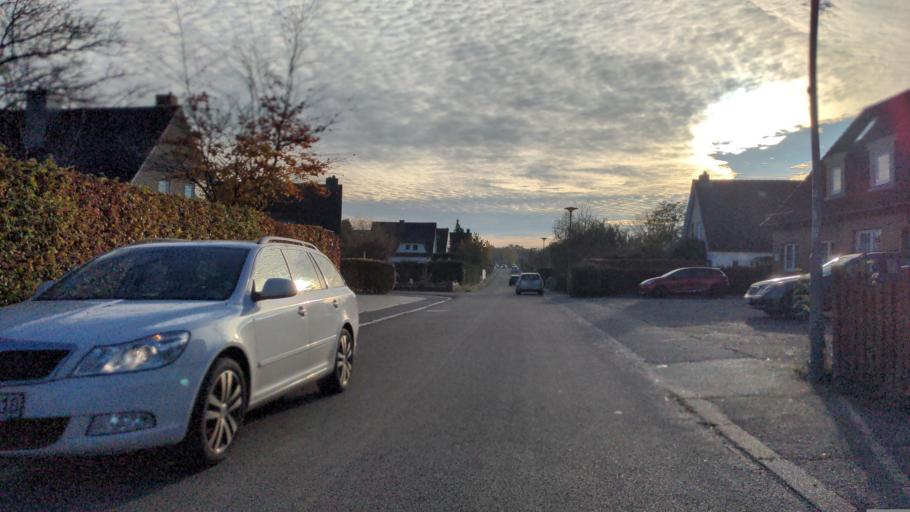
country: DE
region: Schleswig-Holstein
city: Gross Gronau
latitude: 53.8467
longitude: 10.7442
